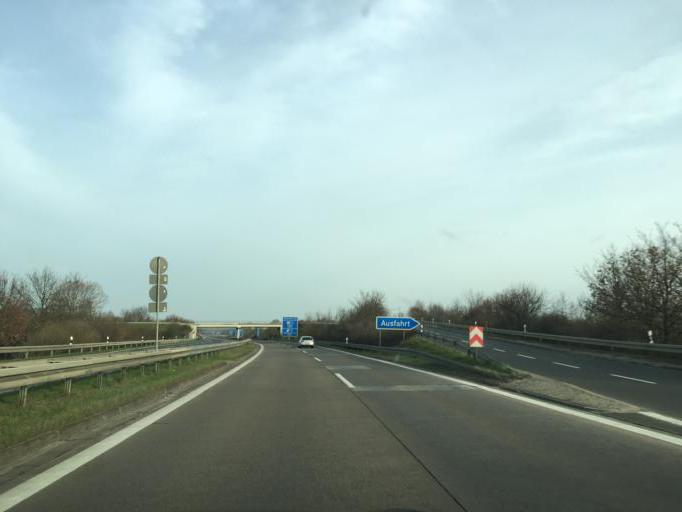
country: DE
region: Berlin
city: Buchholz
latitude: 52.6134
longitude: 13.4465
